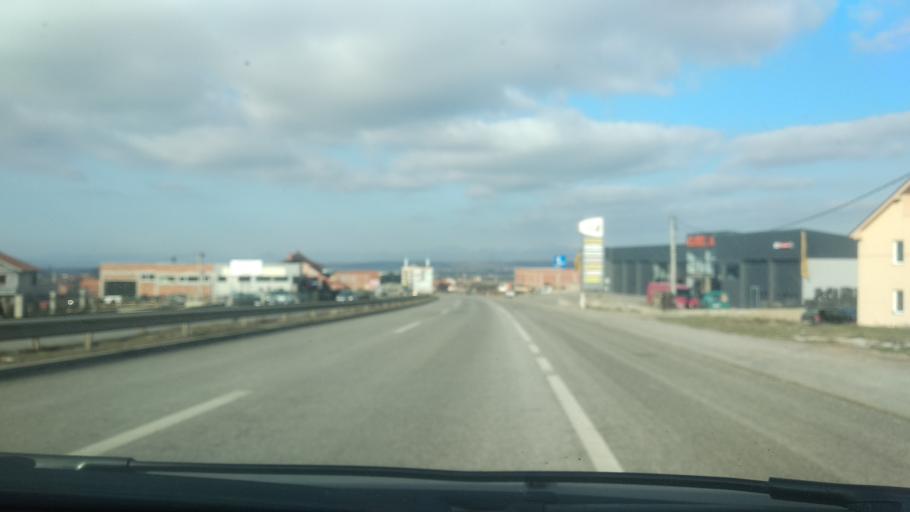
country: XK
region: Pristina
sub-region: Kosovo Polje
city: Kosovo Polje
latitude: 42.6925
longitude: 21.1176
